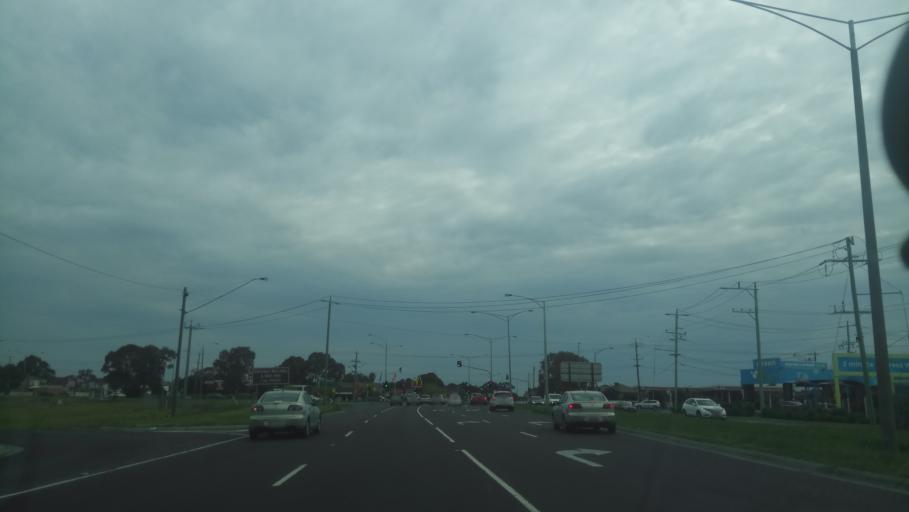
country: AU
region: Victoria
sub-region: Kingston
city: Chelsea Heights
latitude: -38.0270
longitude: 145.1321
